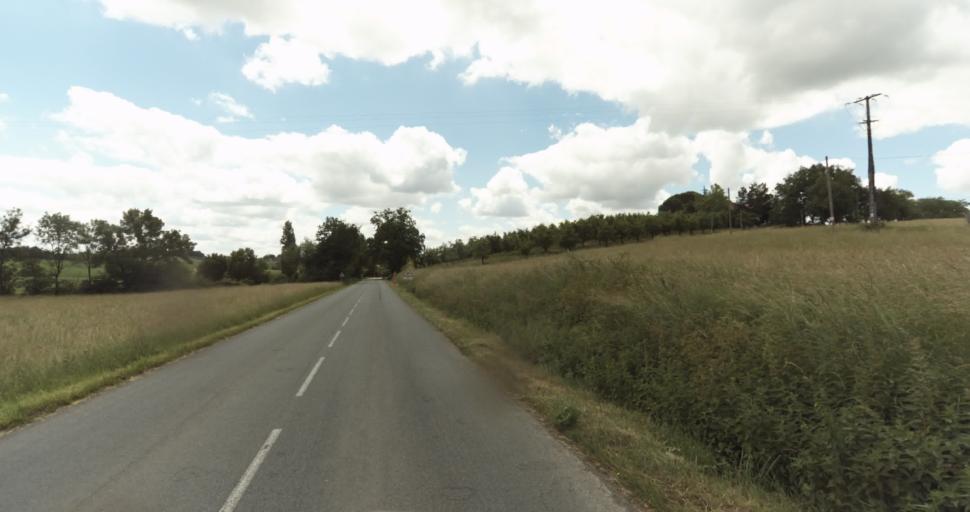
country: FR
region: Aquitaine
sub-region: Departement de la Dordogne
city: Beaumont-du-Perigord
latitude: 44.7050
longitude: 0.7501
